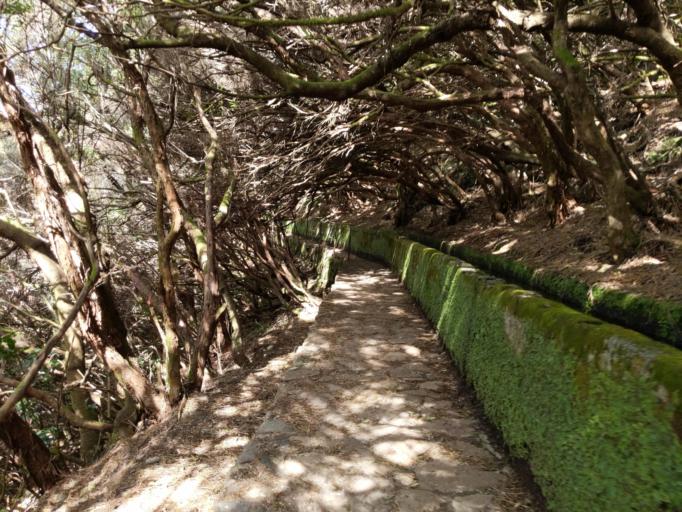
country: PT
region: Madeira
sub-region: Calheta
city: Arco da Calheta
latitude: 32.7655
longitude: -17.1291
